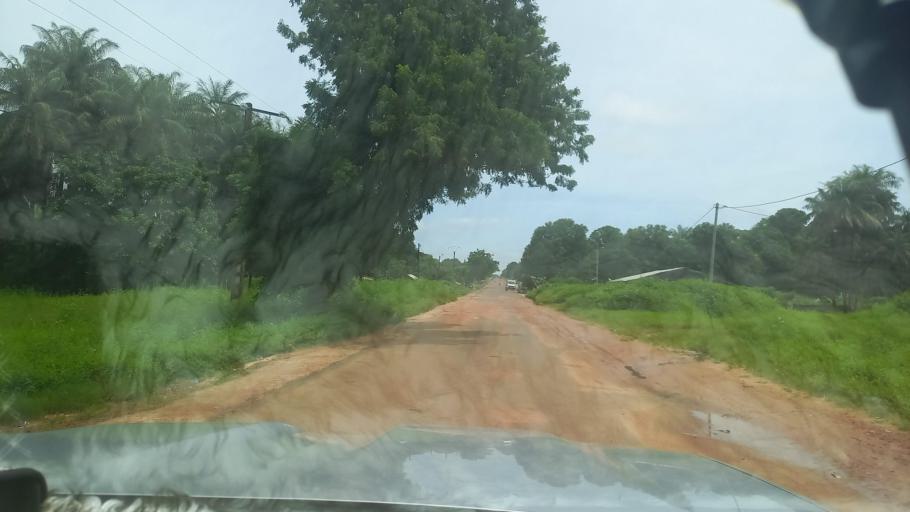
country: SN
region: Kolda
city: Marsassoum
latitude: 12.9671
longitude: -15.9598
